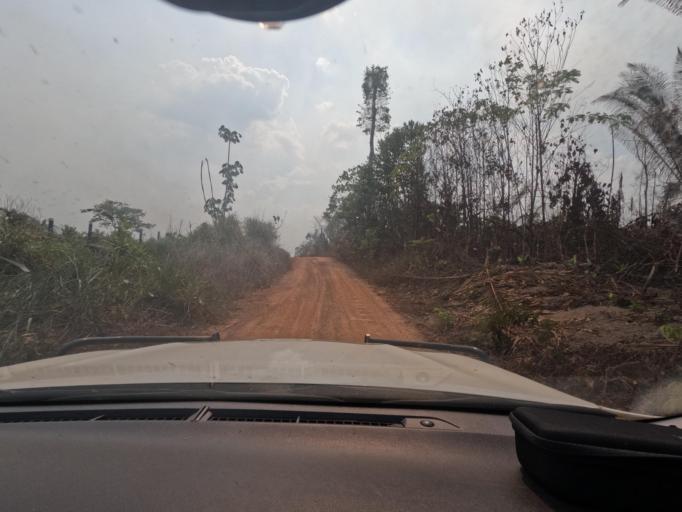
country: BR
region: Rondonia
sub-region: Porto Velho
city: Porto Velho
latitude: -8.7729
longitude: -63.2032
